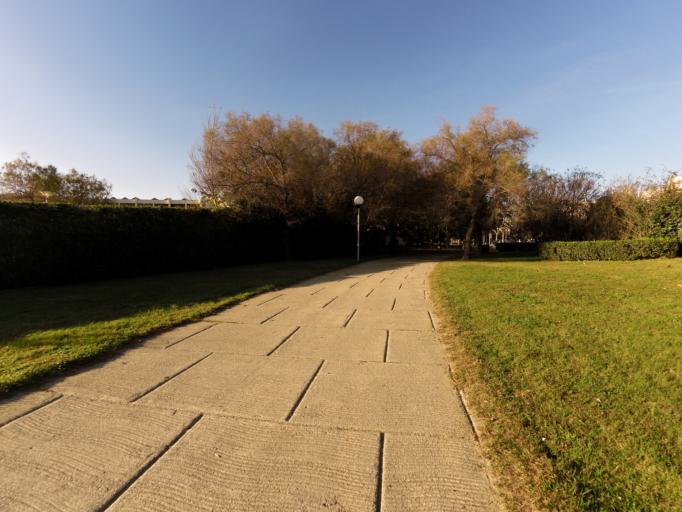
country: FR
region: Languedoc-Roussillon
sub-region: Departement de l'Herault
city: La Grande-Motte
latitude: 43.5590
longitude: 4.0607
